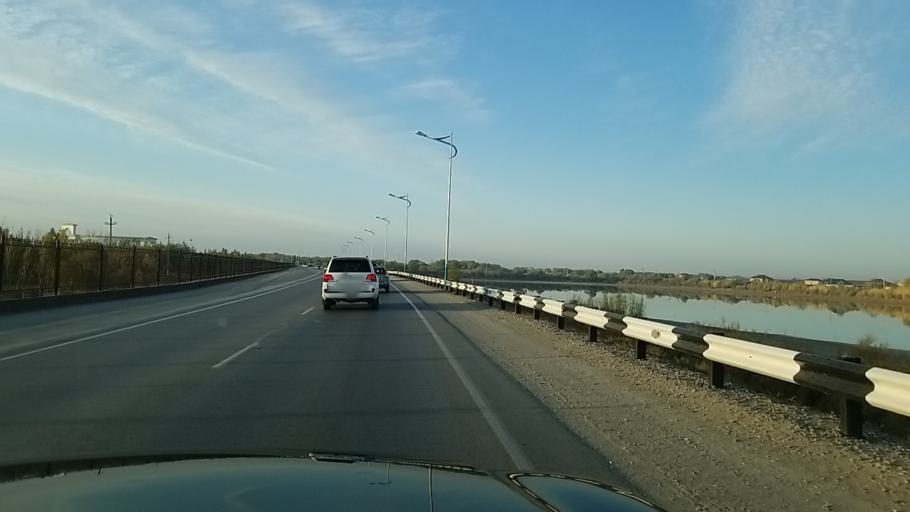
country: KZ
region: Qyzylorda
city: Tasboget
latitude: 44.7781
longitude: 65.5041
